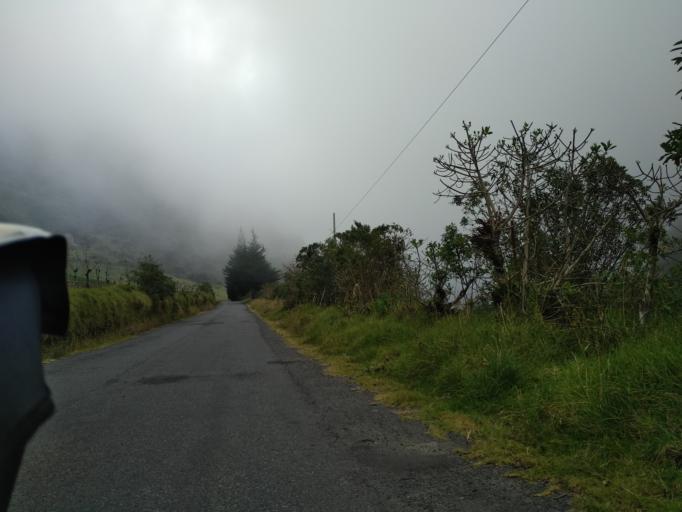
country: EC
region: Cotopaxi
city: Saquisili
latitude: -0.6915
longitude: -78.8238
